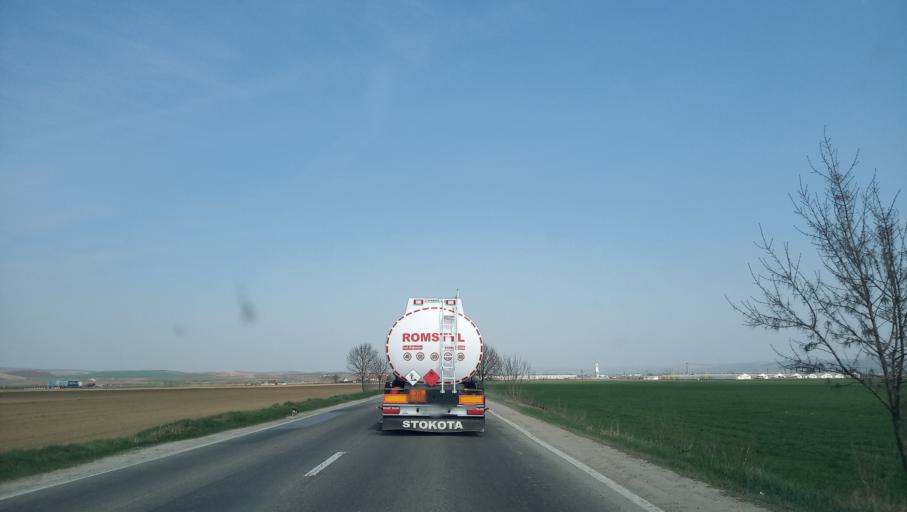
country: RO
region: Alba
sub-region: Comuna Galda de Jos
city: Galda de Jos
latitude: 46.1702
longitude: 23.6507
